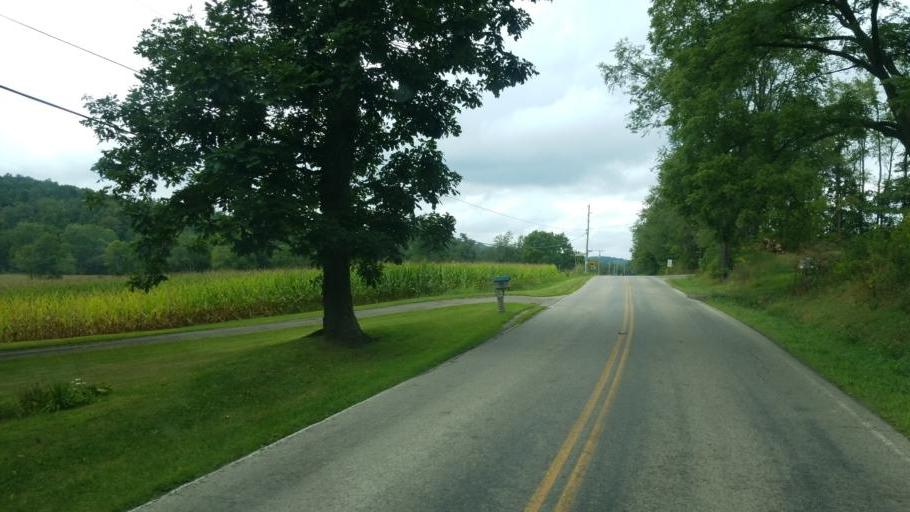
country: US
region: Ohio
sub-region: Sandusky County
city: Bellville
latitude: 40.6472
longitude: -82.4721
